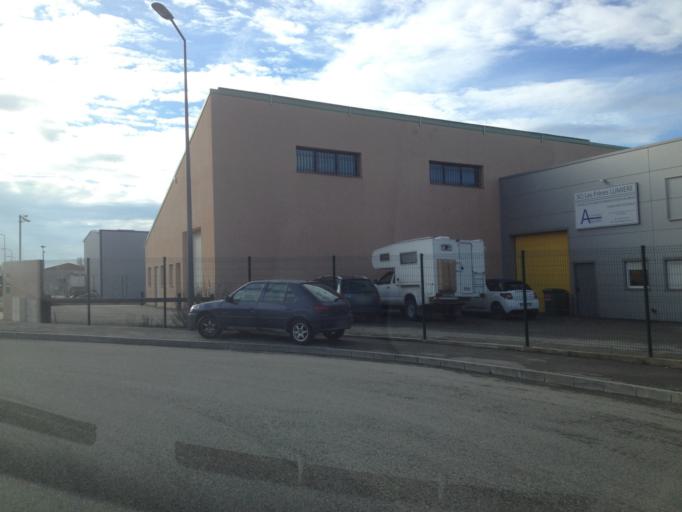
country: FR
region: Provence-Alpes-Cote d'Azur
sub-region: Departement du Vaucluse
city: Bedarrides
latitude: 44.0260
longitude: 4.8863
